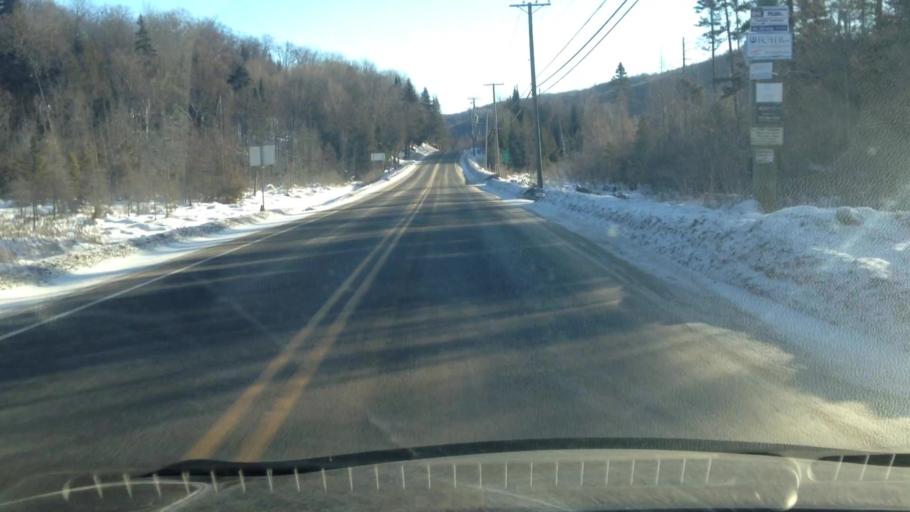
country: CA
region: Quebec
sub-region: Laurentides
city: Saint-Sauveur
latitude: 45.9045
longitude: -74.3138
